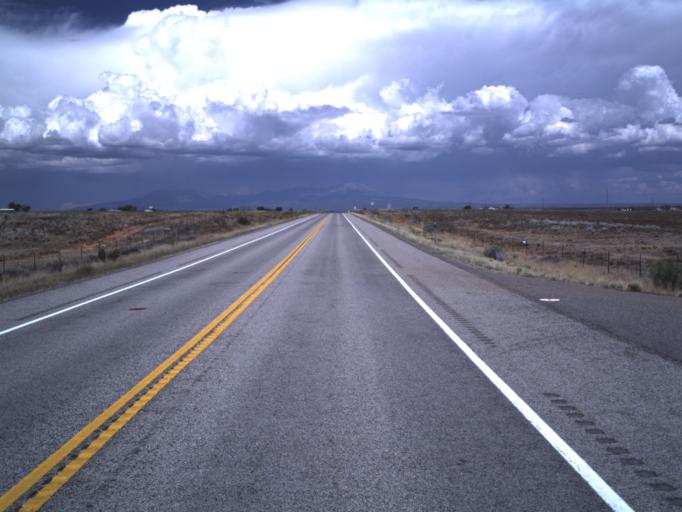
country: US
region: Utah
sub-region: San Juan County
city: Blanding
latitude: 37.4511
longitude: -109.4671
